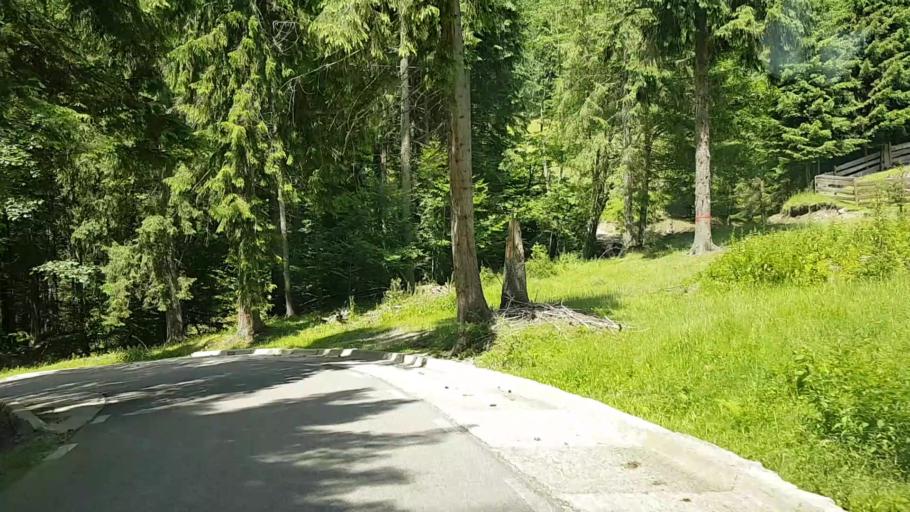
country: RO
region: Suceava
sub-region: Comuna Crucea
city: Crucea
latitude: 47.4253
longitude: 25.5769
